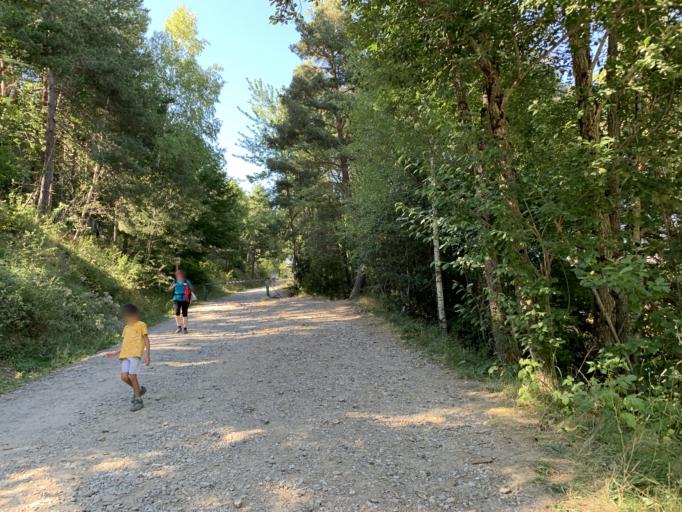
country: ES
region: Aragon
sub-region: Provincia de Huesca
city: Hoz de Jaca
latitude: 42.6971
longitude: -0.3338
